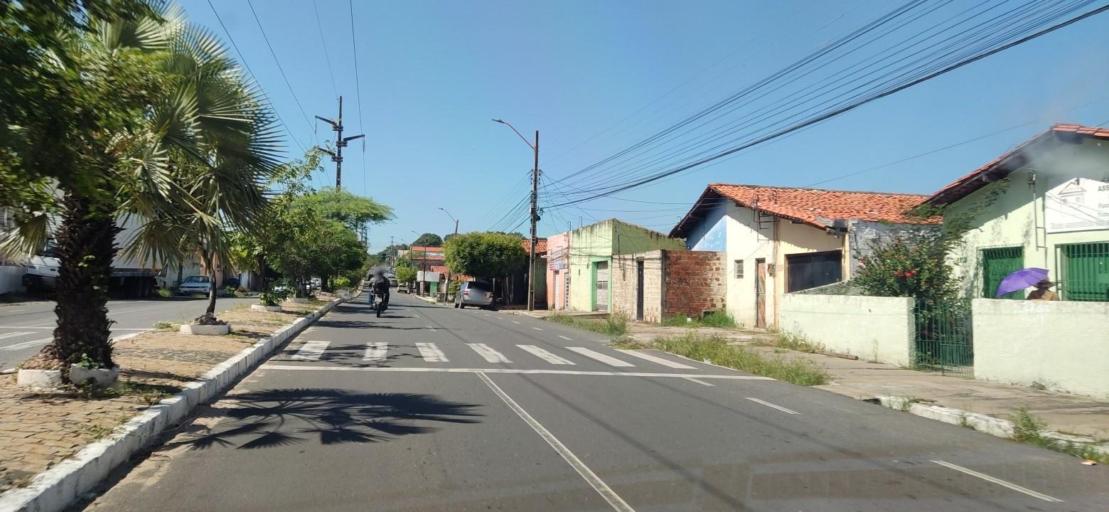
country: BR
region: Piaui
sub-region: Teresina
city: Teresina
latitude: -5.1186
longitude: -42.8102
